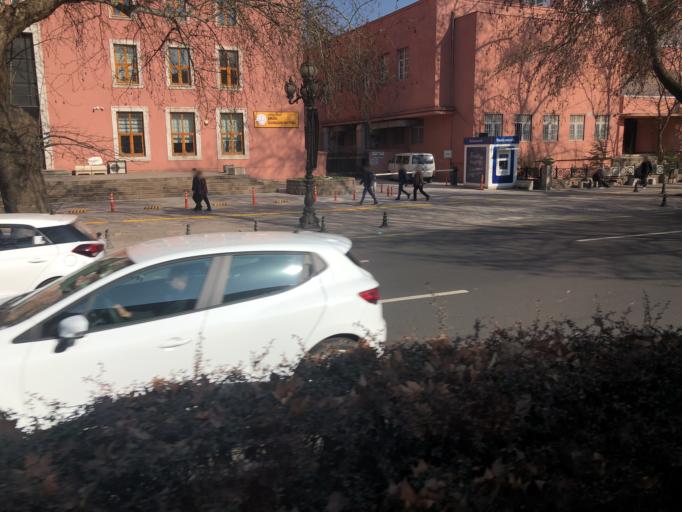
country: TR
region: Ankara
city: Ankara
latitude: 39.9318
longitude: 32.8537
